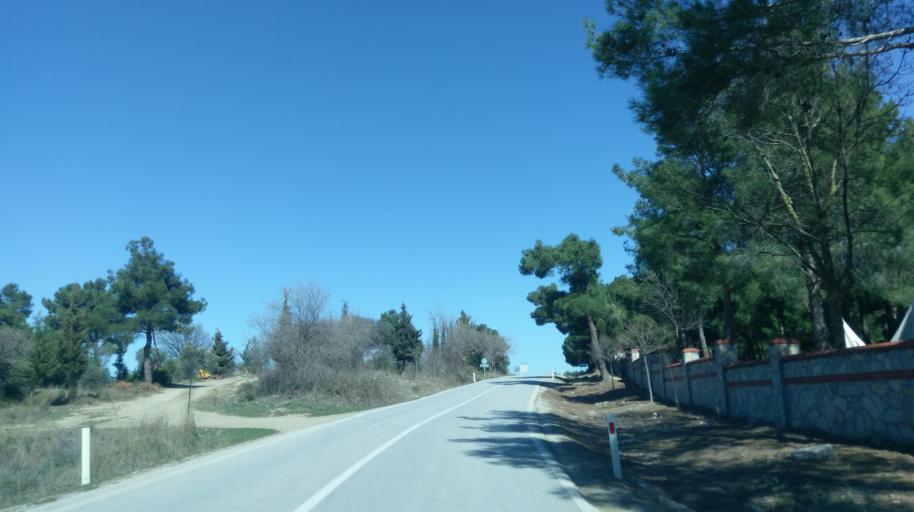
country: TR
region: Canakkale
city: Intepe
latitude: 40.0981
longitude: 26.2269
